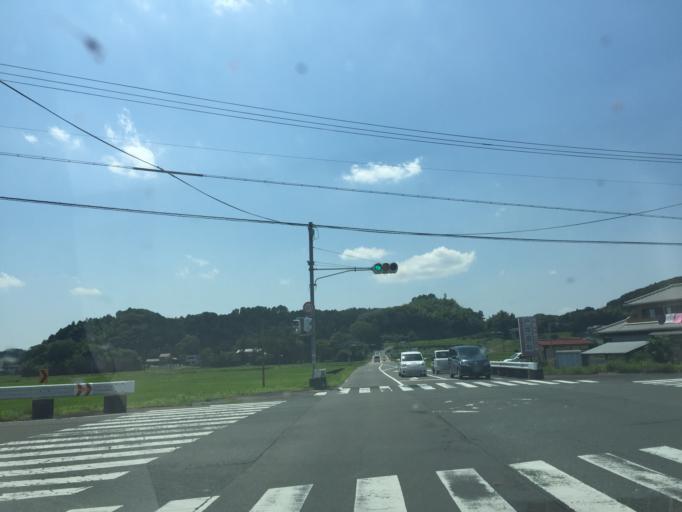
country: JP
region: Shizuoka
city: Kakegawa
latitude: 34.7973
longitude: 137.9914
